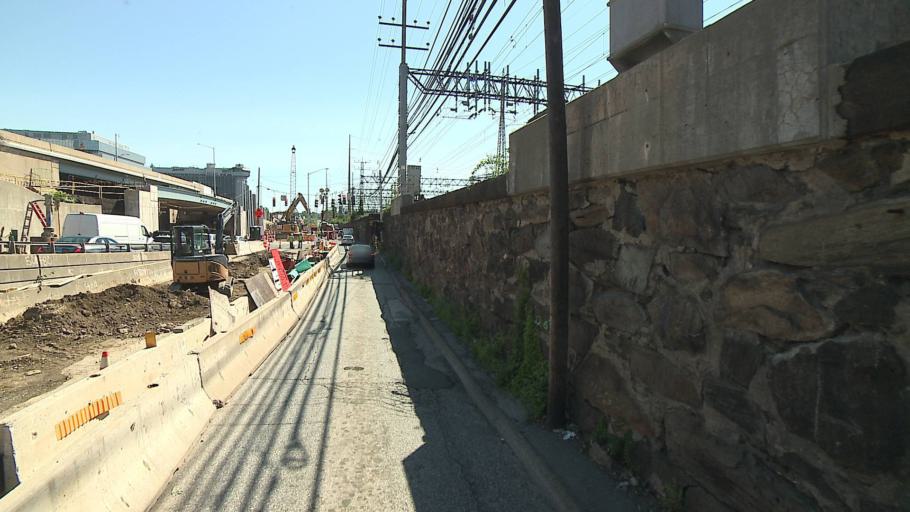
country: US
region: Connecticut
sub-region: Fairfield County
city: Stamford
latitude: 41.0478
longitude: -73.5399
